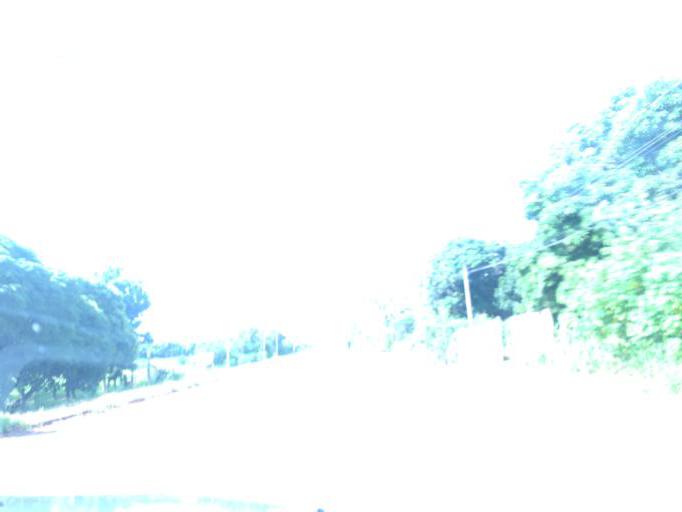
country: BR
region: Federal District
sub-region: Brasilia
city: Brasilia
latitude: -15.7417
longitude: -48.1254
